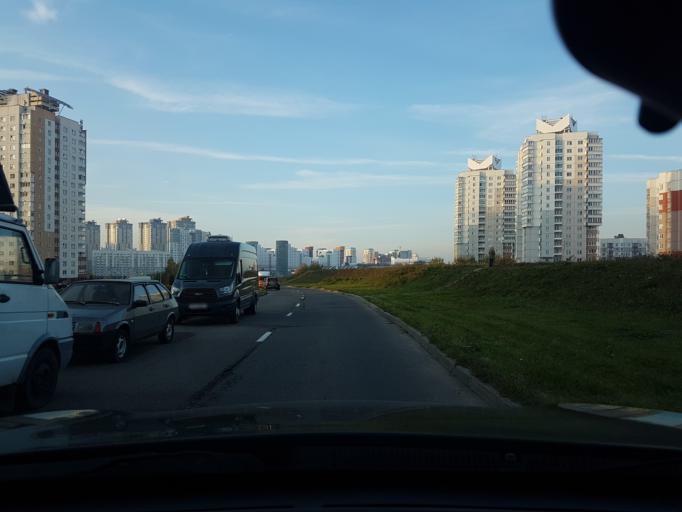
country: BY
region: Minsk
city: Yubilyeyny
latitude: 53.8490
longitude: 27.4904
